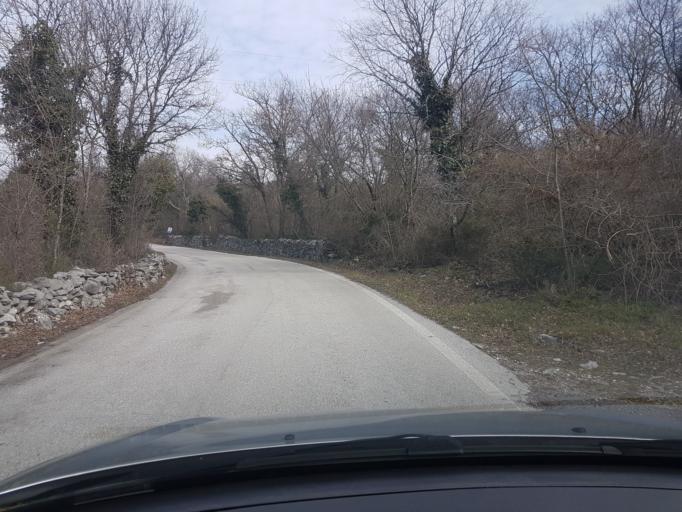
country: IT
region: Friuli Venezia Giulia
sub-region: Provincia di Trieste
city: Aurisina Cave
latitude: 45.7719
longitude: 13.6676
